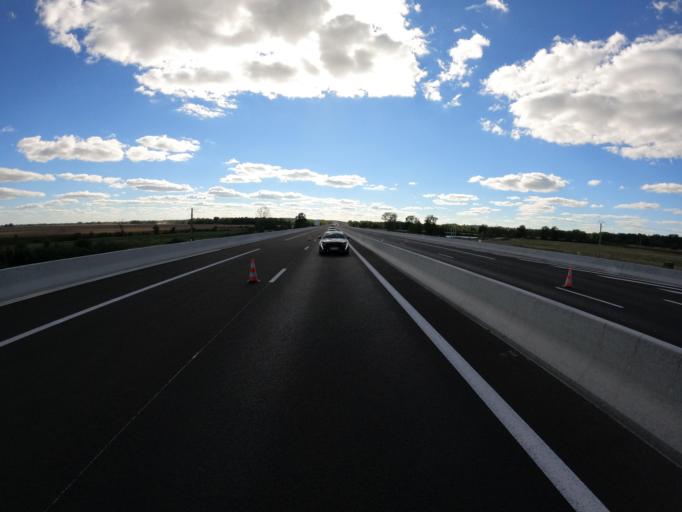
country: FR
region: Auvergne
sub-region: Departement de l'Allier
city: Toulon-sur-Allier
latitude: 46.4859
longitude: 3.3400
